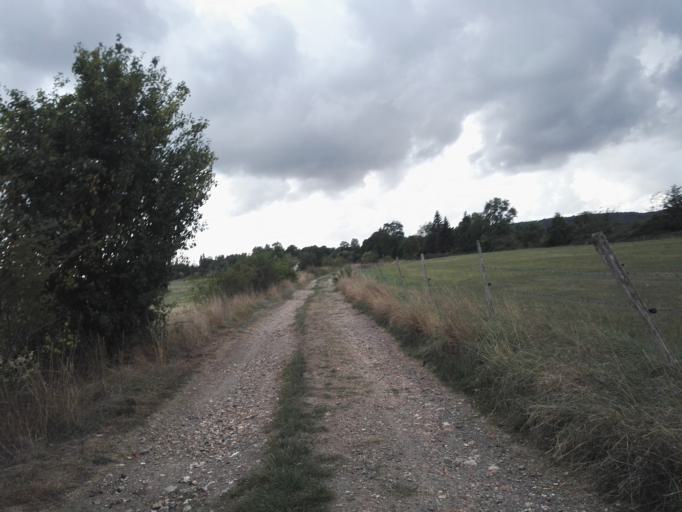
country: FR
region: Haute-Normandie
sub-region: Departement de l'Eure
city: Menilles
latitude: 49.0482
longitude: 1.3406
